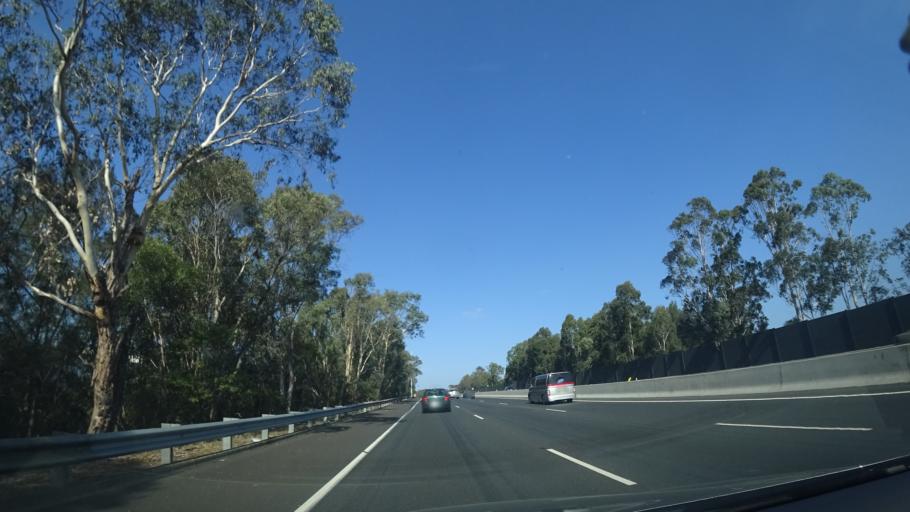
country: AU
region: New South Wales
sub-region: Canterbury
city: Roselands
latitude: -33.9432
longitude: 151.0590
